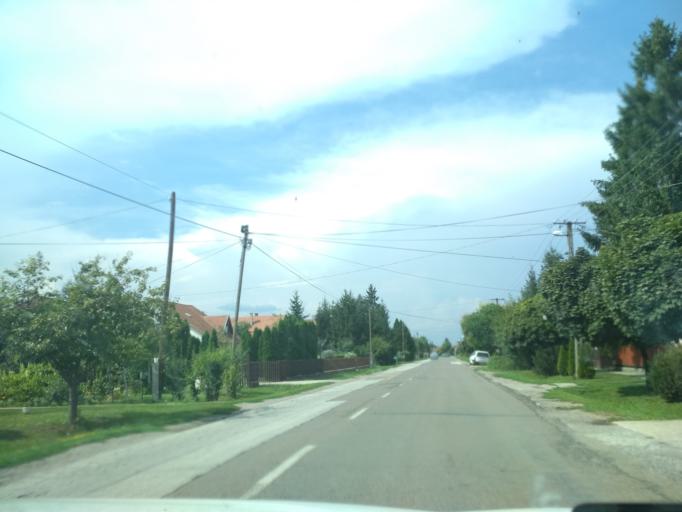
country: HU
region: Jasz-Nagykun-Szolnok
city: Tiszaszolos
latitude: 47.5507
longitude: 20.7206
